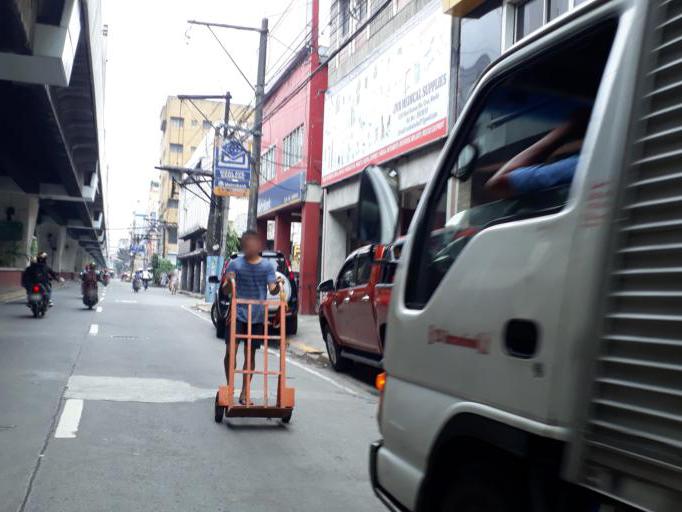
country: PH
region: Metro Manila
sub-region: City of Manila
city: Manila
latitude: 14.6107
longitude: 120.9825
